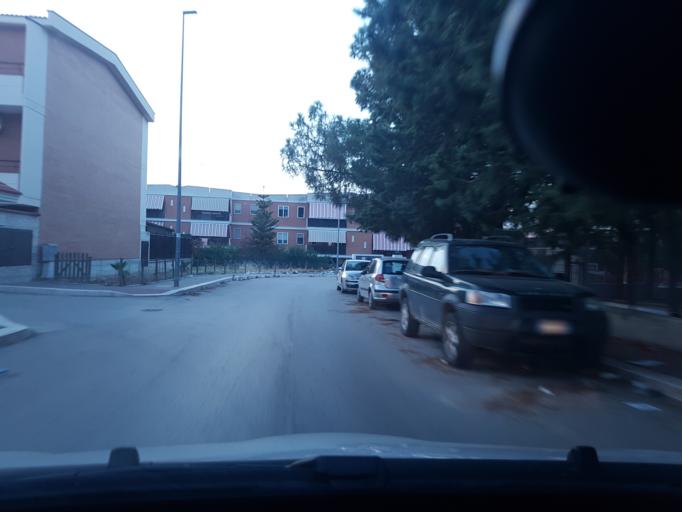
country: IT
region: Apulia
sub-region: Provincia di Foggia
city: Cerignola
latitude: 41.2614
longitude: 15.8797
